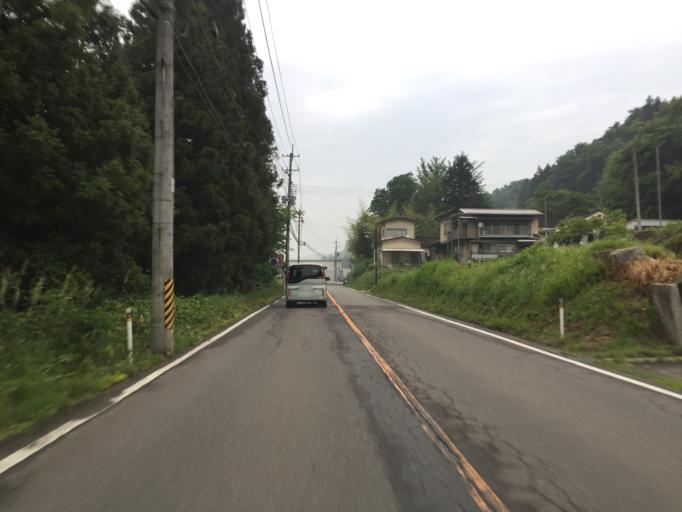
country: JP
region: Fukushima
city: Ishikawa
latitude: 37.1599
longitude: 140.4685
